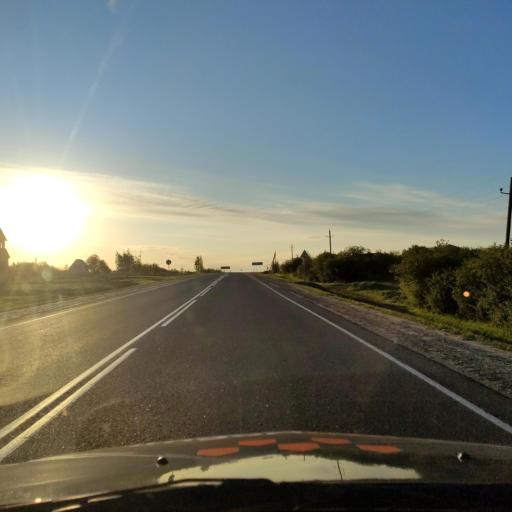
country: RU
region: Orjol
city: Livny
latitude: 52.4494
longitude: 37.6238
